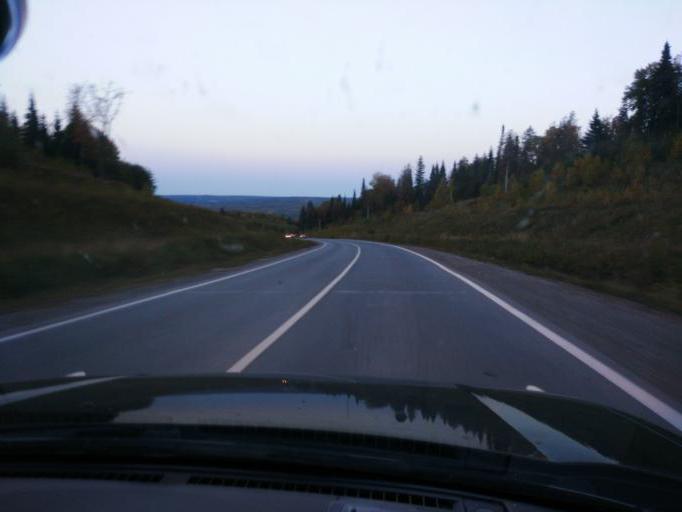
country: RU
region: Perm
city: Sylva
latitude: 58.2918
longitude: 56.8242
